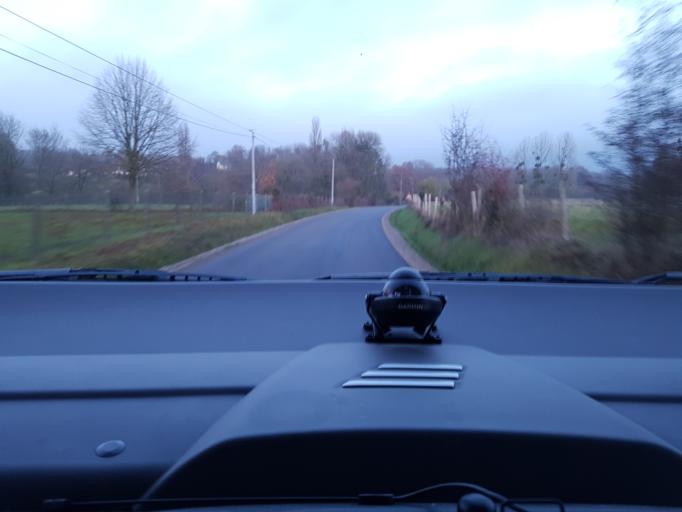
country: FR
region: Lower Normandy
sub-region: Departement de l'Orne
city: Tourouvre
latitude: 48.6044
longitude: 0.6839
